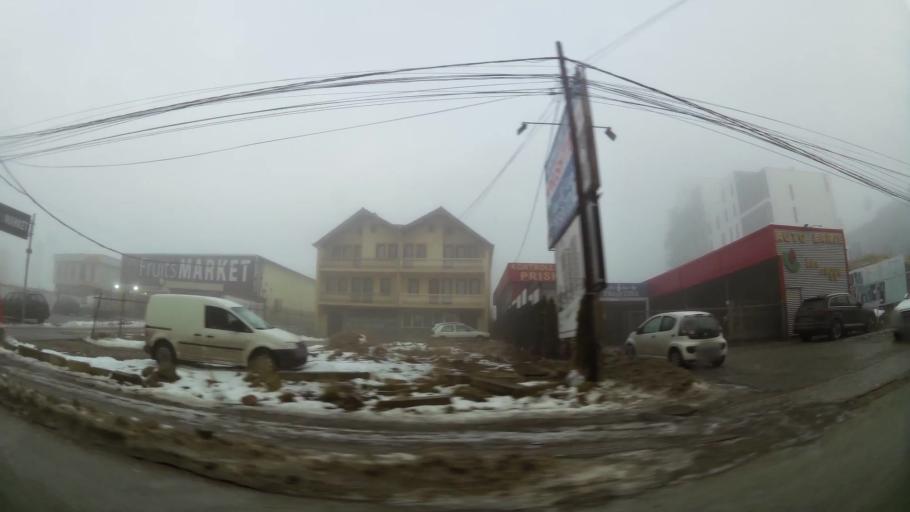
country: XK
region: Pristina
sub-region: Komuna e Prishtines
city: Pristina
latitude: 42.6582
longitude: 21.1461
